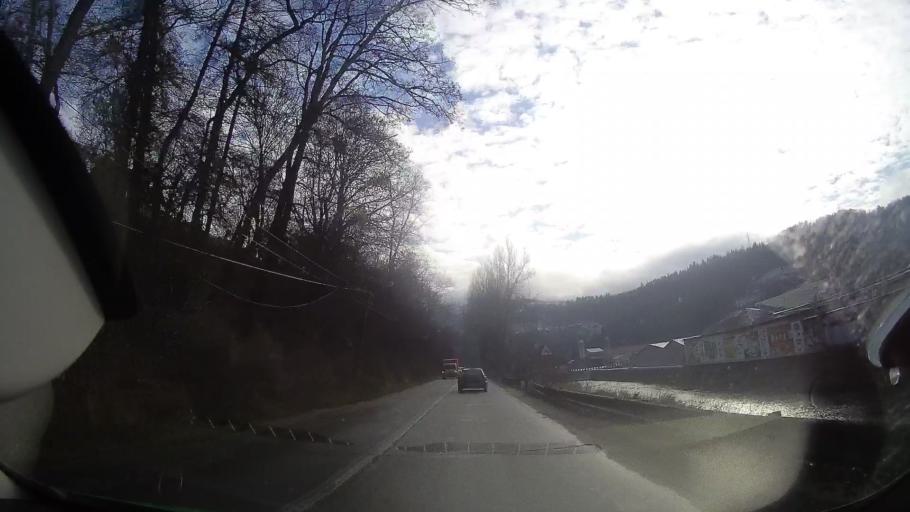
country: RO
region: Alba
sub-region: Oras Campeni
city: Campeni
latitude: 46.3623
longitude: 23.0600
